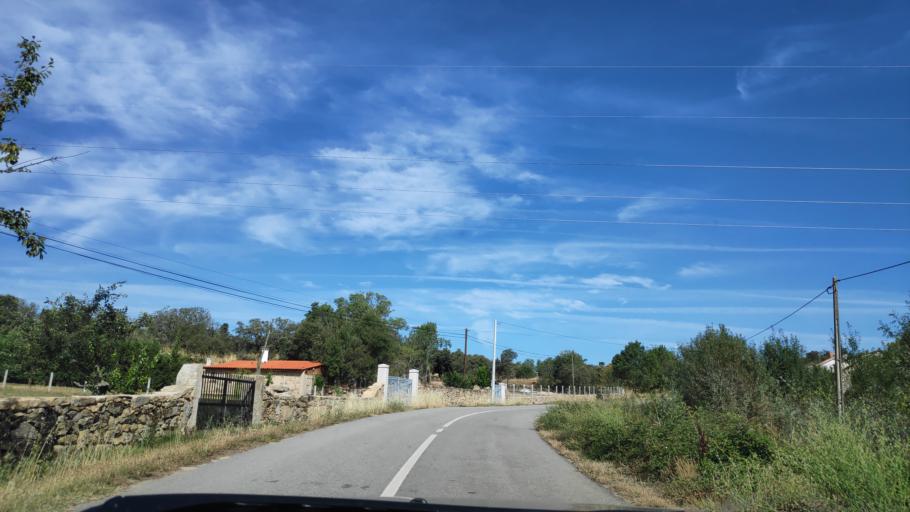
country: ES
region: Castille and Leon
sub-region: Provincia de Zamora
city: Fariza
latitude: 41.4321
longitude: -6.3490
